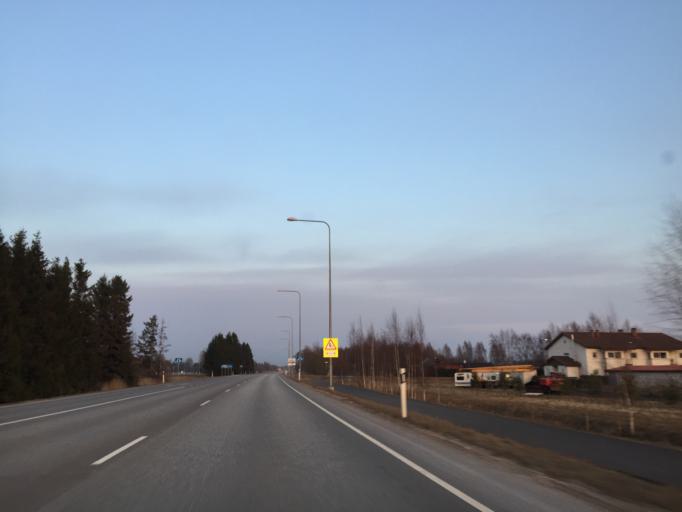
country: EE
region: Paernumaa
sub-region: Audru vald
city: Audru
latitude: 58.4009
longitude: 24.4287
